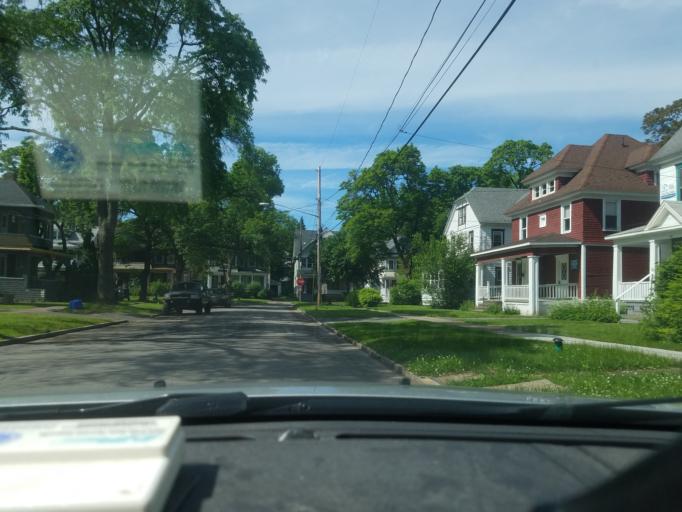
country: US
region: New York
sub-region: Onondaga County
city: Syracuse
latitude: 43.0378
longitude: -76.1204
